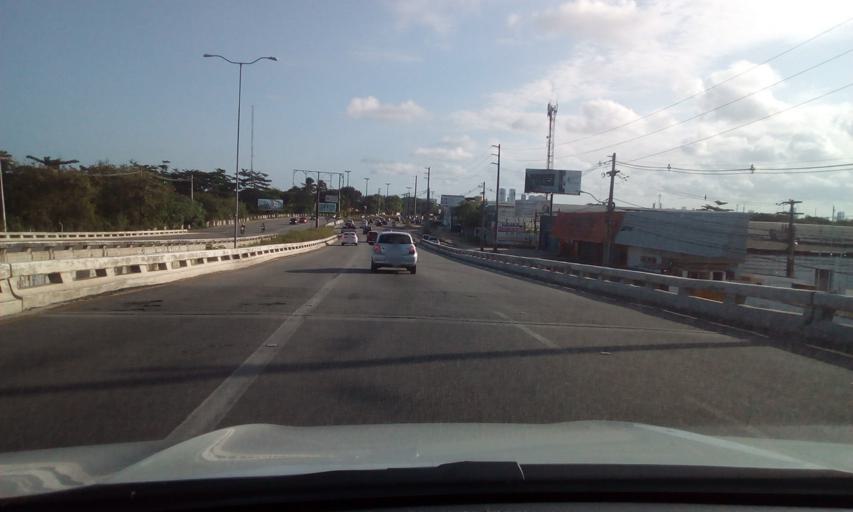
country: BR
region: Pernambuco
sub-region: Olinda
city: Olinda
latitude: -8.0203
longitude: -34.8612
